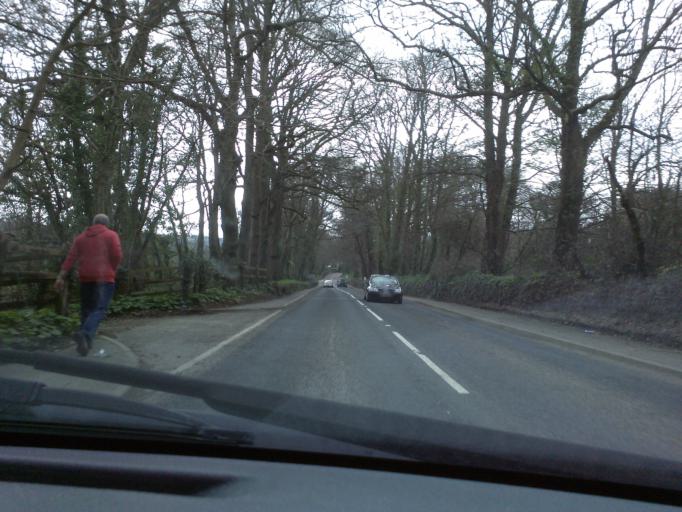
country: GB
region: England
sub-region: Cornwall
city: Penzance
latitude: 50.1111
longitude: -5.5614
